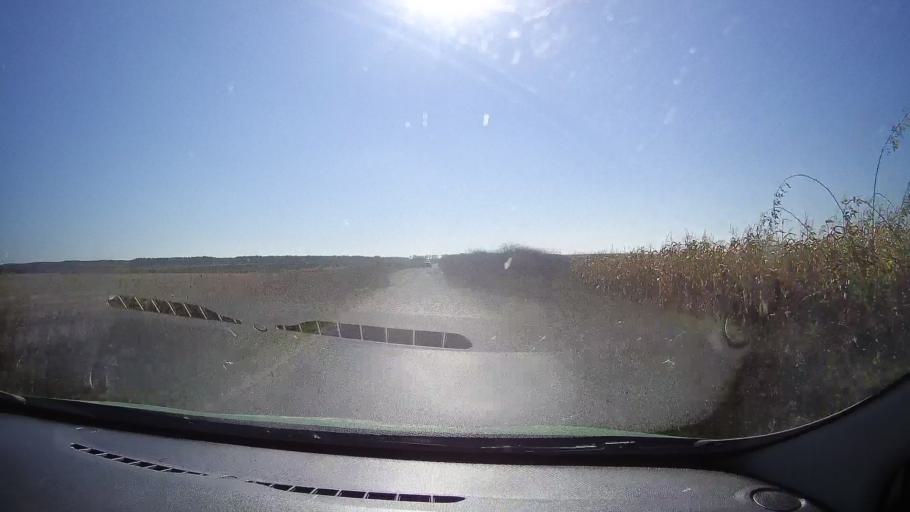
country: RO
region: Satu Mare
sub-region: Comuna Doba
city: Doba
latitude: 47.7287
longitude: 22.7242
